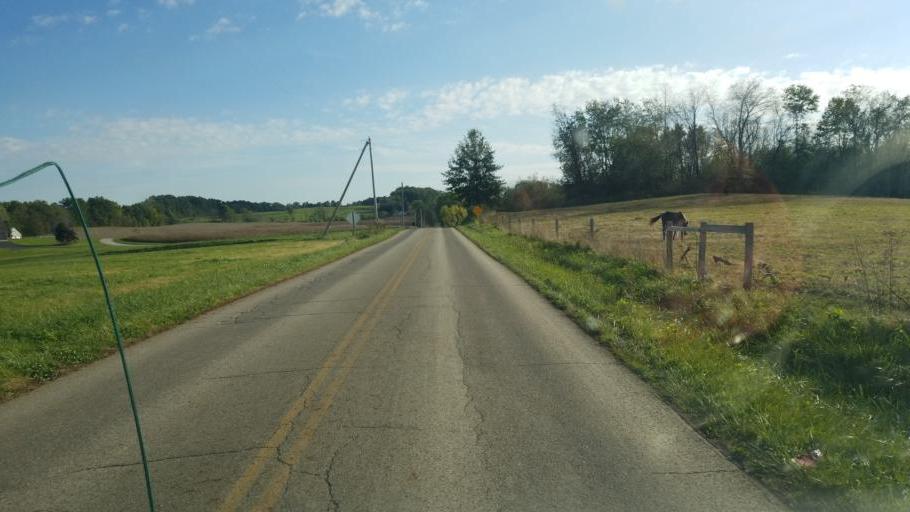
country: US
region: Ohio
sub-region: Wayne County
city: Shreve
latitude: 40.6457
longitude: -82.0816
